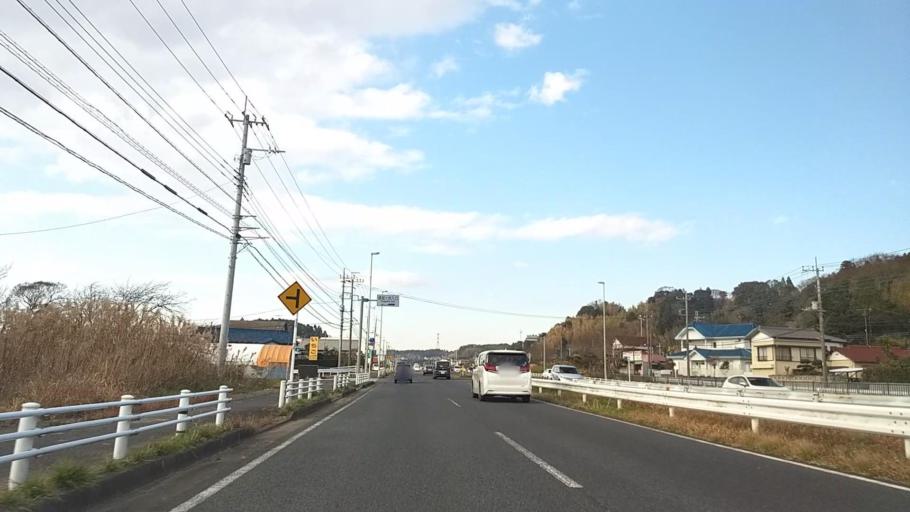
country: JP
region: Chiba
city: Togane
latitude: 35.5645
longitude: 140.3371
